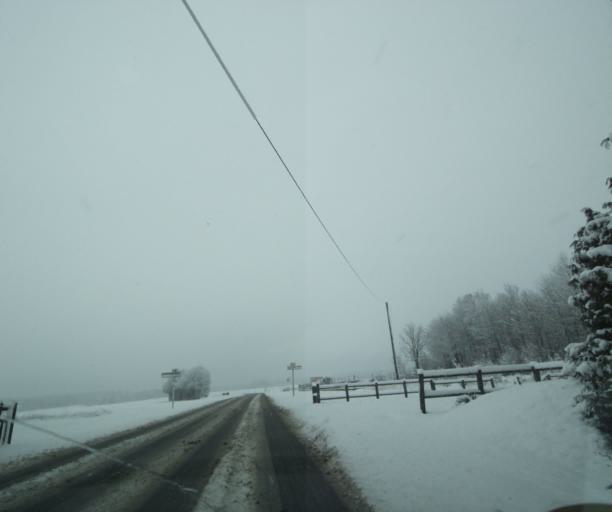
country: FR
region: Champagne-Ardenne
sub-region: Departement de la Haute-Marne
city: Saint-Dizier
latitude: 48.5884
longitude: 4.9019
